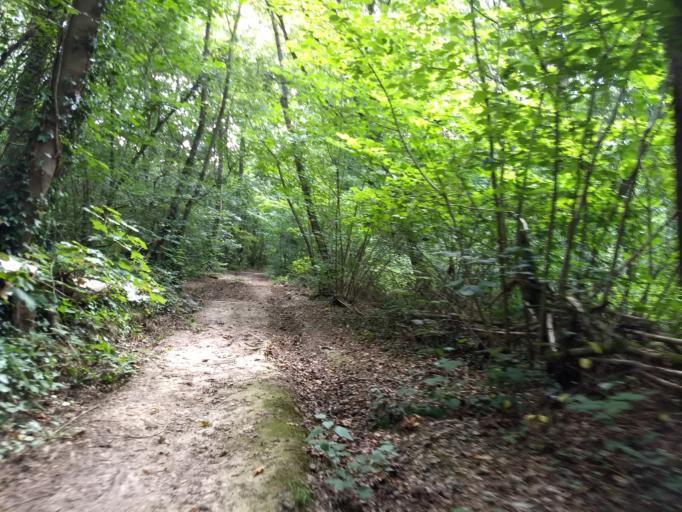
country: GB
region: England
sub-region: Isle of Wight
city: Newport
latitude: 50.7176
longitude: -1.2594
